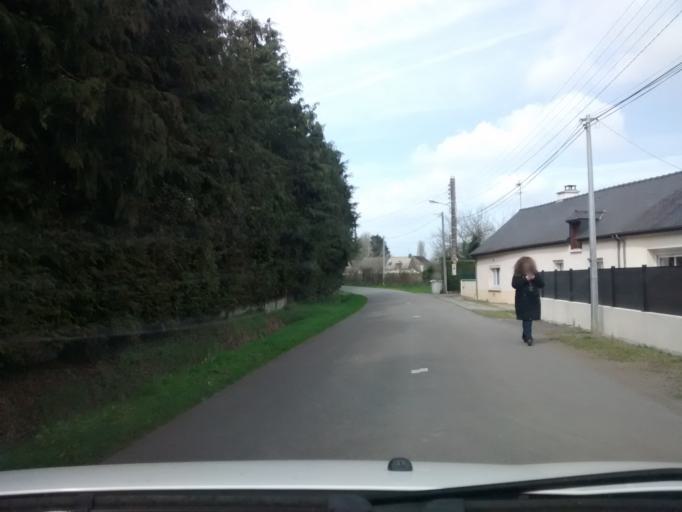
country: FR
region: Brittany
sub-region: Departement d'Ille-et-Vilaine
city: Bruz
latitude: 48.0405
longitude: -1.7479
